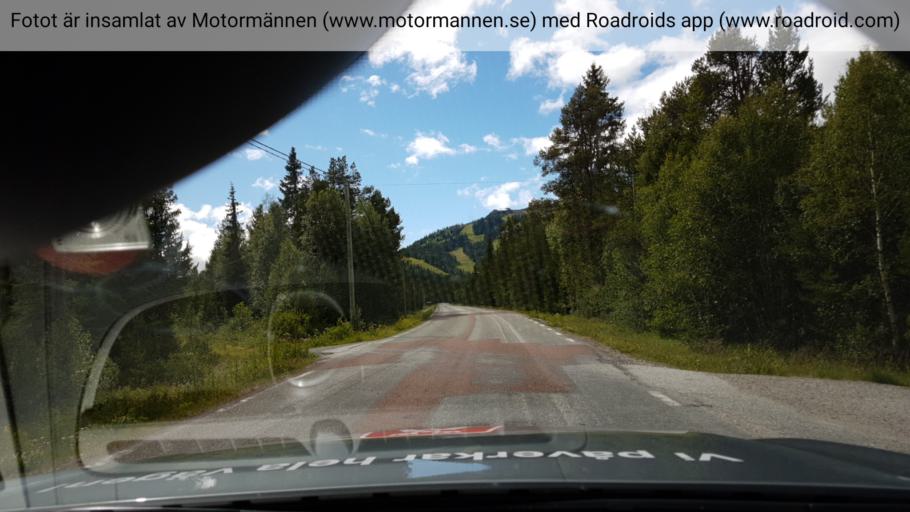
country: SE
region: Jaemtland
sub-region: Are Kommun
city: Are
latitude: 62.5498
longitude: 12.5921
